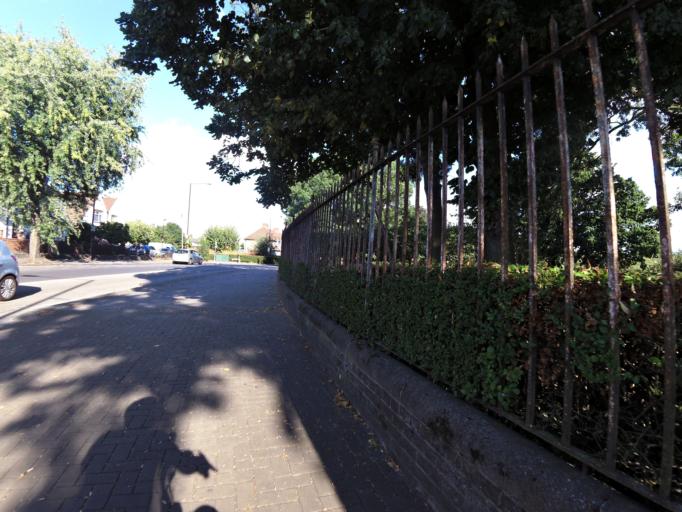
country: GB
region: England
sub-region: Greater London
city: Harringay
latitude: 51.6051
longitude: -0.0828
